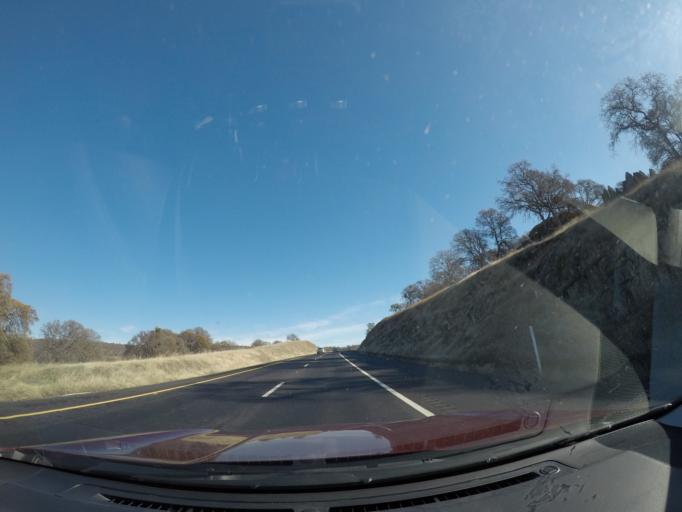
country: US
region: California
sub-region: Calaveras County
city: Copperopolis
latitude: 37.8452
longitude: -120.6135
